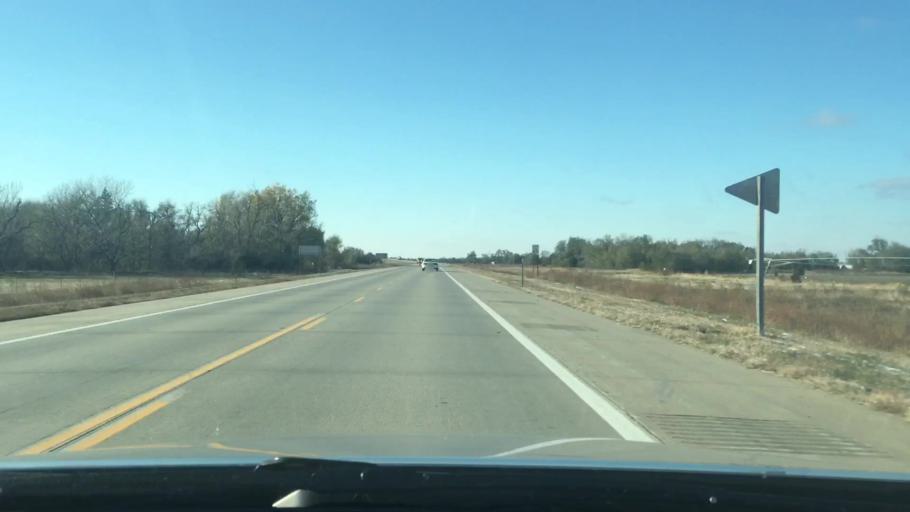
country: US
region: Kansas
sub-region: Reno County
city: Hutchinson
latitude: 38.0964
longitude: -98.0044
